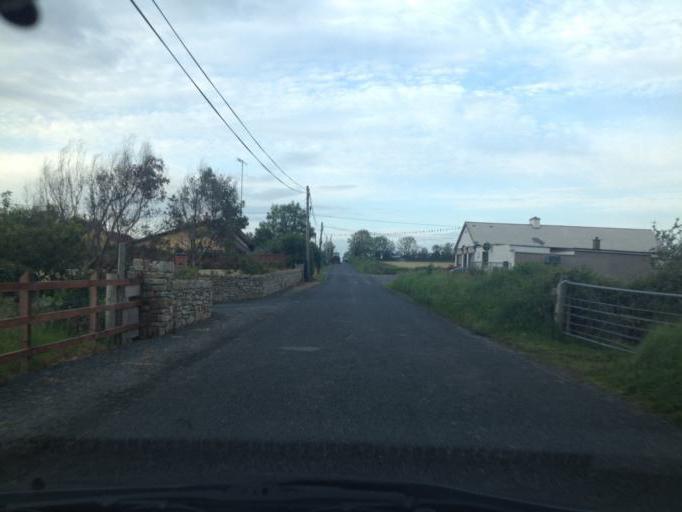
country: IE
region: Connaught
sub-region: Sligo
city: Strandhill
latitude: 54.3772
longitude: -8.5684
